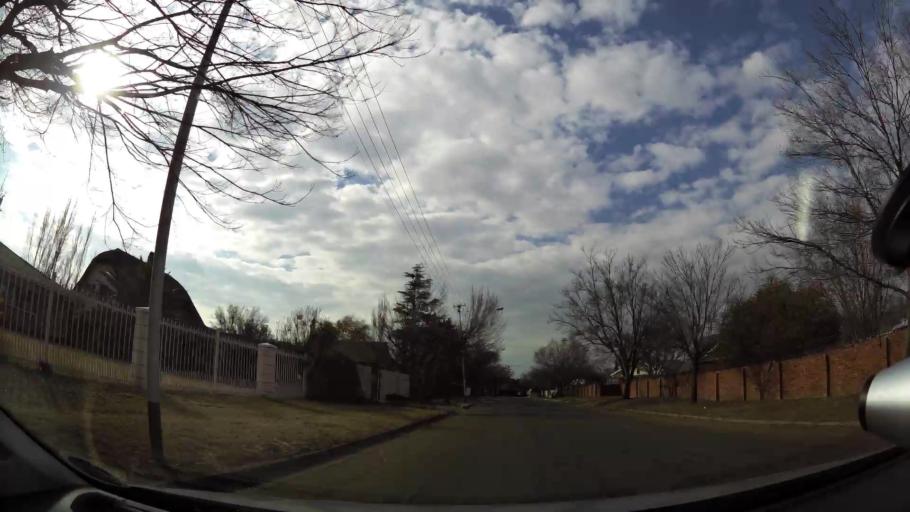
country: ZA
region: Orange Free State
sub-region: Mangaung Metropolitan Municipality
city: Bloemfontein
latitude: -29.0863
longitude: 26.2343
